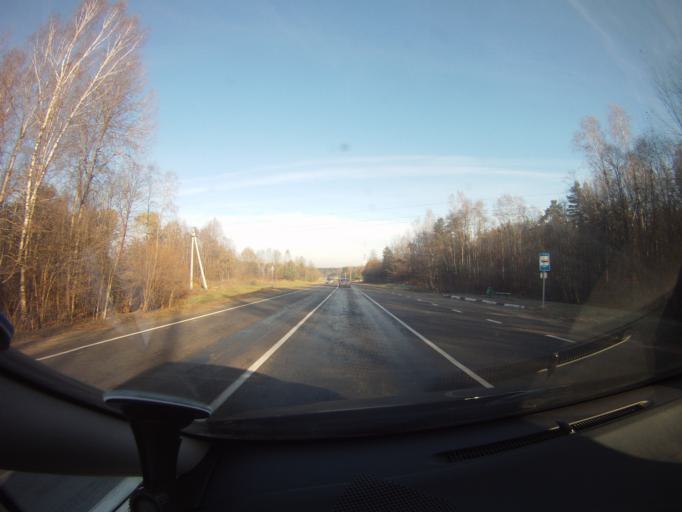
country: BY
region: Minsk
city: Syomkava
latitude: 54.1620
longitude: 27.5018
